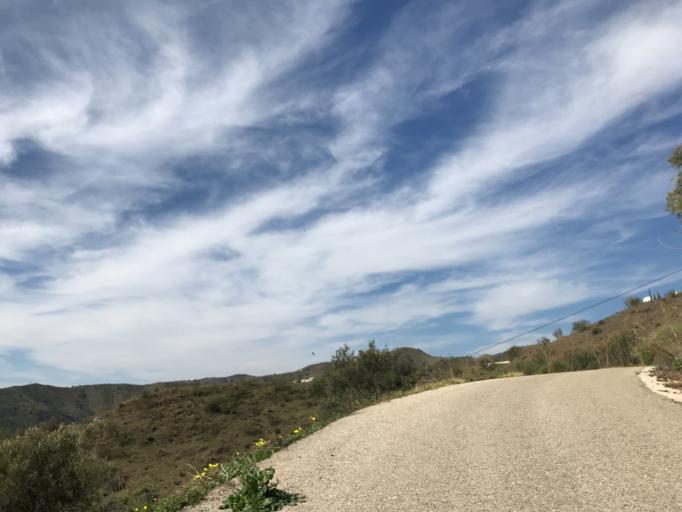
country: ES
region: Andalusia
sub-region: Provincia de Malaga
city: Valdes
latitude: 36.7736
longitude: -4.2157
